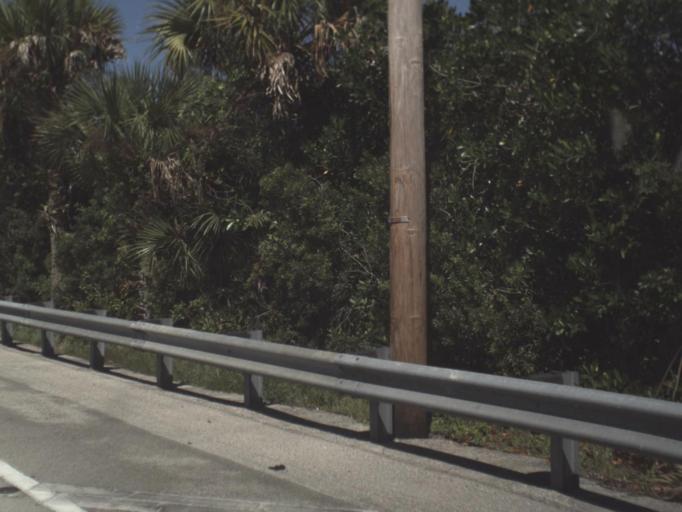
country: US
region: Florida
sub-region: Collier County
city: Marco
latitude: 25.9637
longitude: -81.5240
